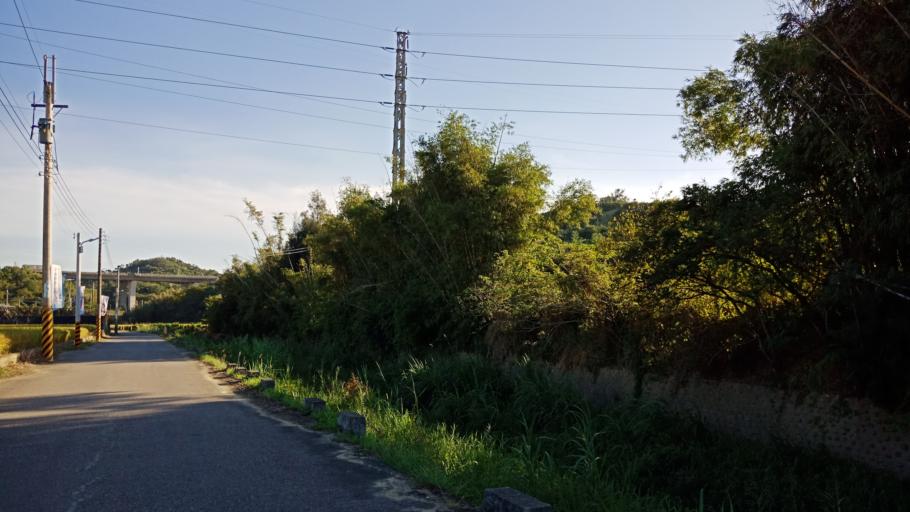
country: TW
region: Taiwan
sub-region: Miaoli
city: Miaoli
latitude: 24.4873
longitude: 120.6967
